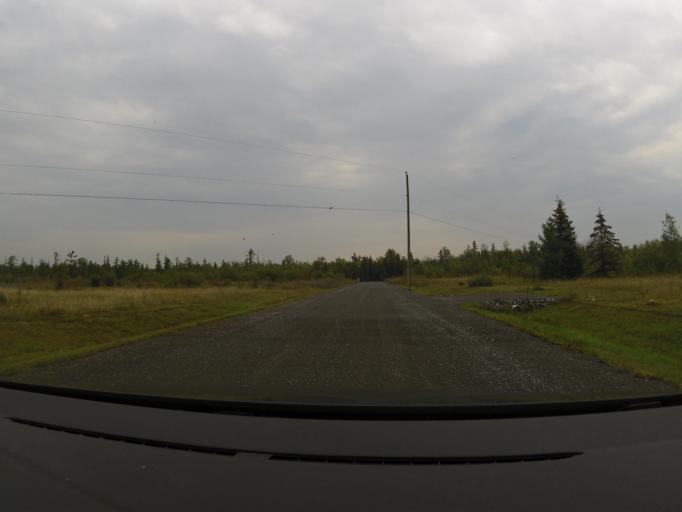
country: CA
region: Ontario
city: Carleton Place
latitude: 45.2456
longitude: -76.1456
